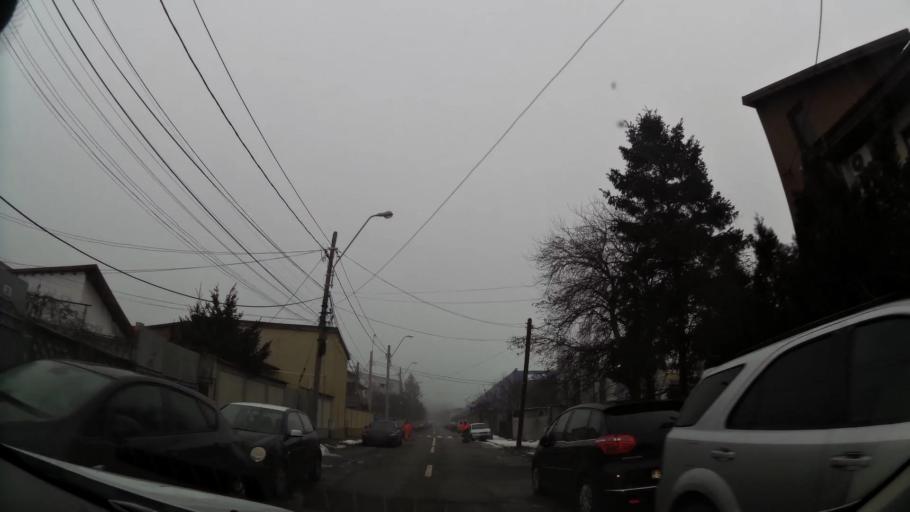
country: RO
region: Ilfov
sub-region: Comuna Chiajna
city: Rosu
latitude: 44.4741
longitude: 26.0437
